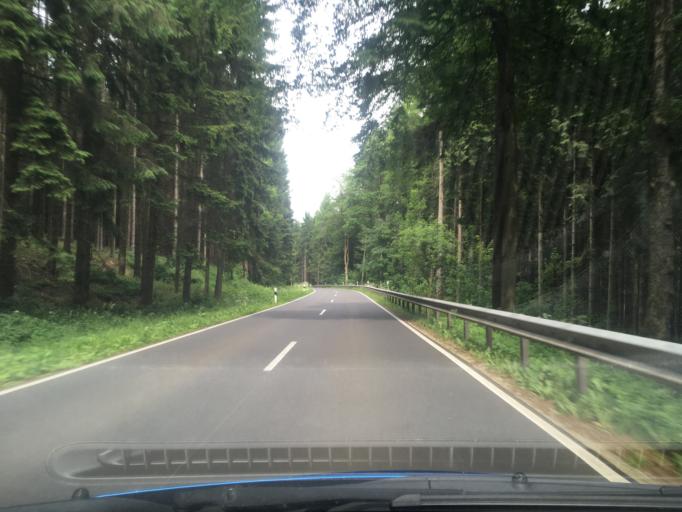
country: DE
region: Lower Saxony
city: Dassel
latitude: 51.7662
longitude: 9.6859
